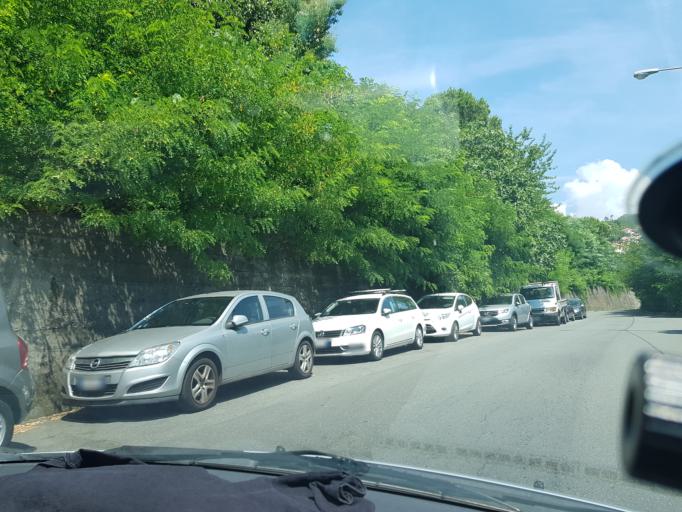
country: IT
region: Liguria
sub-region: Provincia di Genova
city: San Teodoro
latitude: 44.4343
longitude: 8.8412
